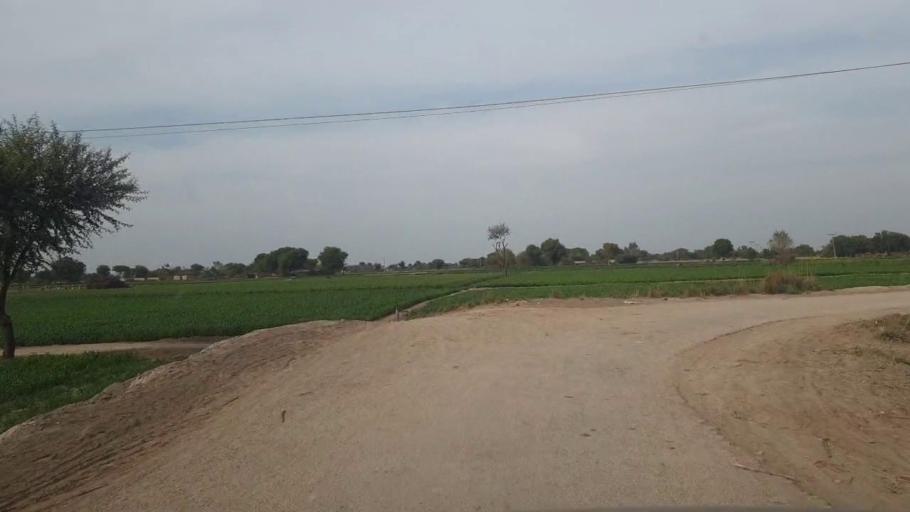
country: PK
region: Sindh
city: Shahpur Chakar
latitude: 26.1108
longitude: 68.5191
